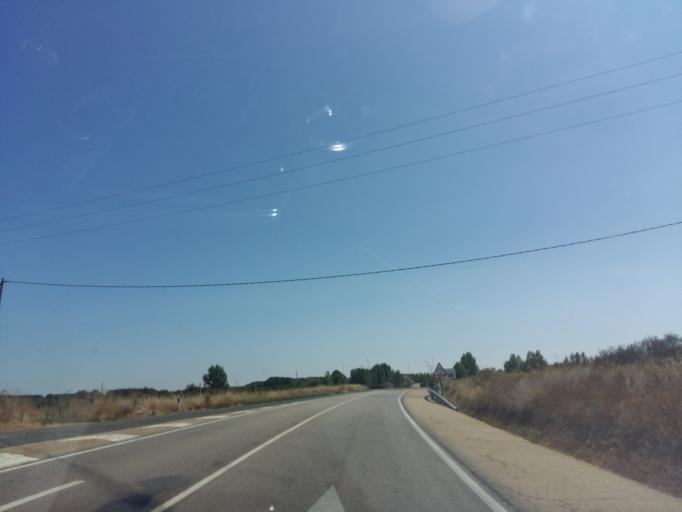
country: ES
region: Castille and Leon
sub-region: Provincia de Leon
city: San Justo de la Vega
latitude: 42.4374
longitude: -6.0341
